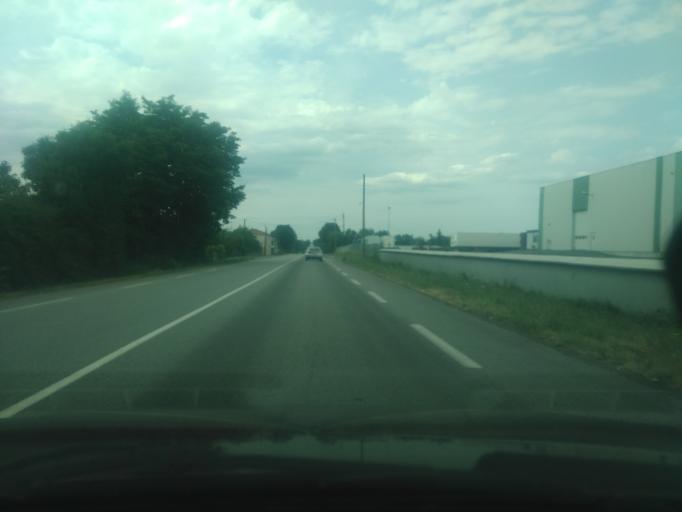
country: FR
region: Pays de la Loire
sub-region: Departement de la Vendee
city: Chantonnay
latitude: 46.7058
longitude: -1.0628
